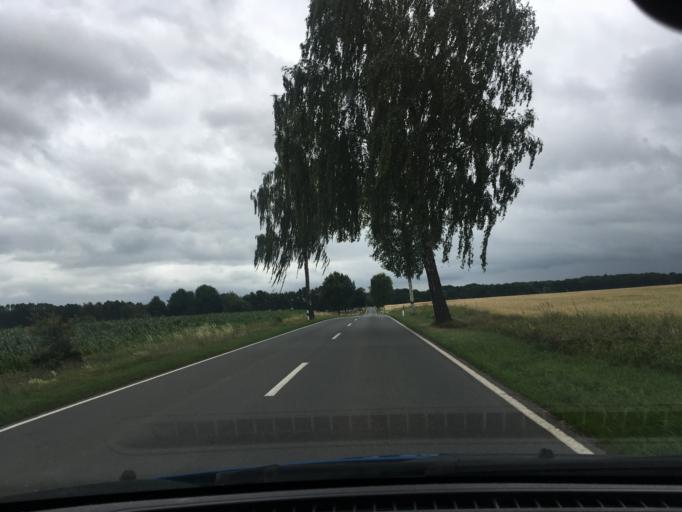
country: DE
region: Lower Saxony
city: Toppenstedt
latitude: 53.2594
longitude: 10.1037
